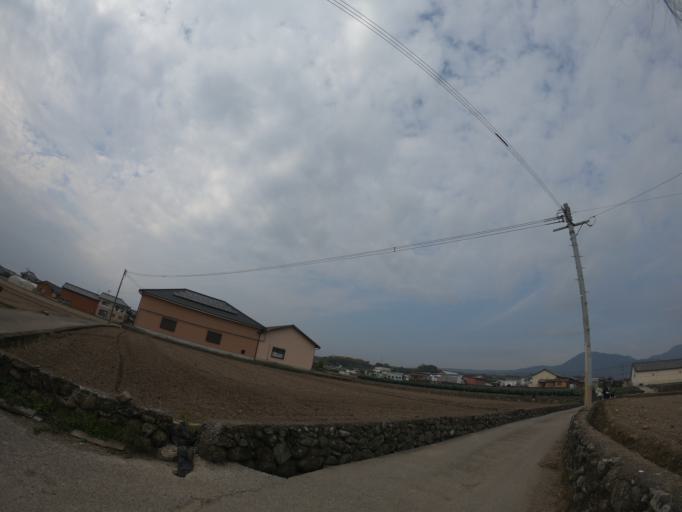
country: JP
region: Nagasaki
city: Shimabara
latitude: 32.6595
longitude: 130.3033
